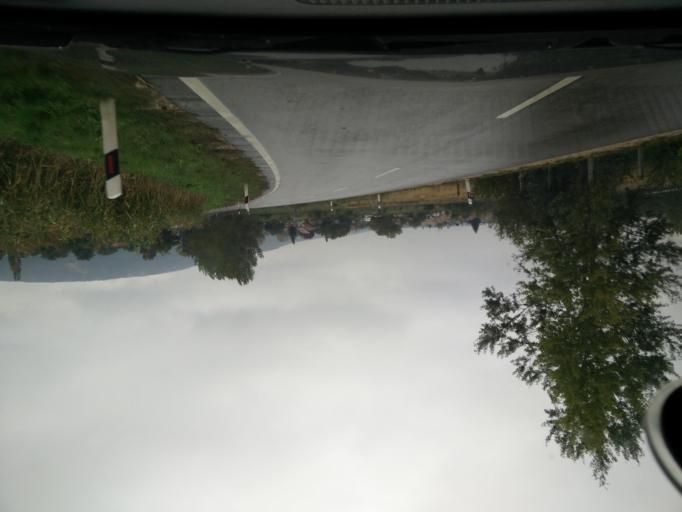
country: HU
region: Komarom-Esztergom
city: Tarjan
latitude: 47.6396
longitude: 18.5143
